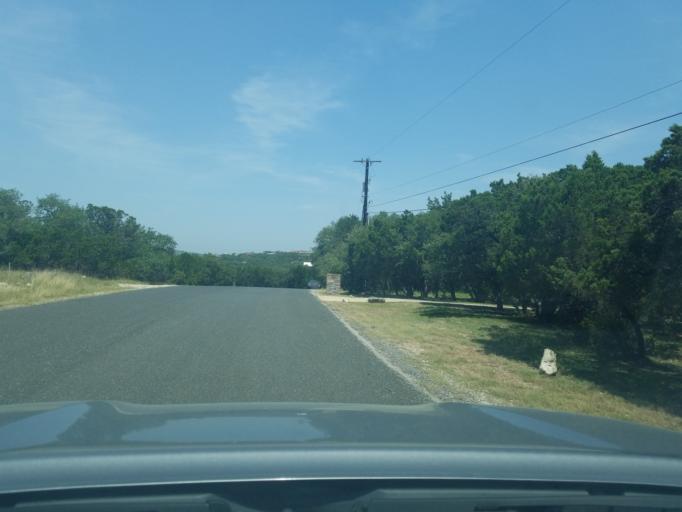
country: US
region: Texas
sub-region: Bexar County
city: Timberwood Park
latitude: 29.6717
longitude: -98.5106
